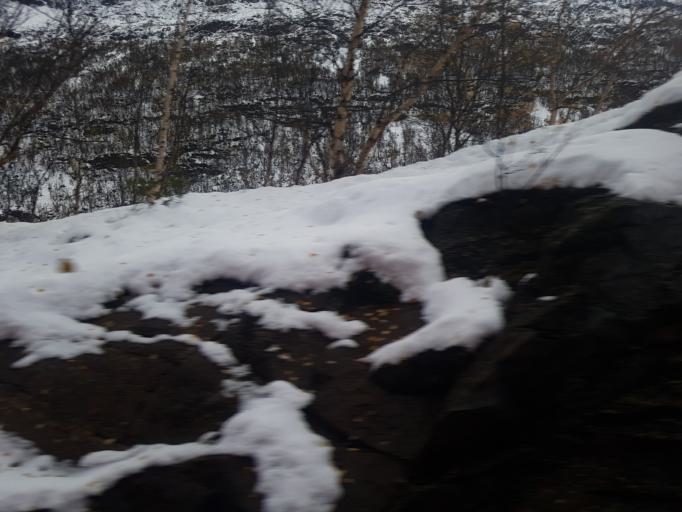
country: NO
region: Sor-Trondelag
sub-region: Oppdal
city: Oppdal
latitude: 62.3382
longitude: 9.6224
